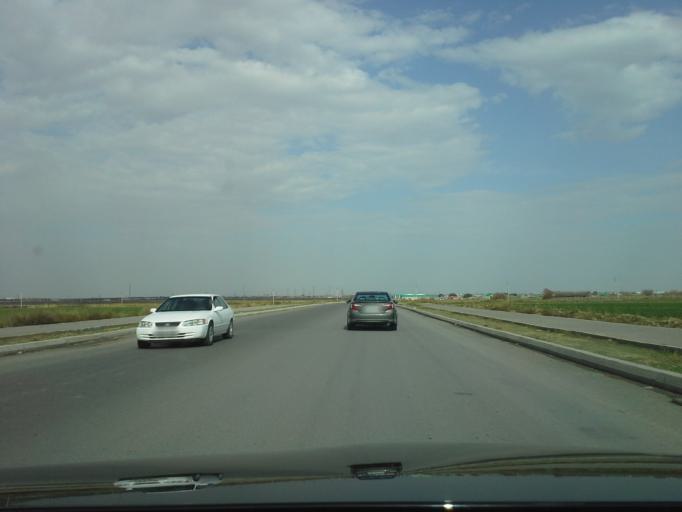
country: TM
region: Ahal
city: Abadan
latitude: 37.9837
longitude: 58.2654
